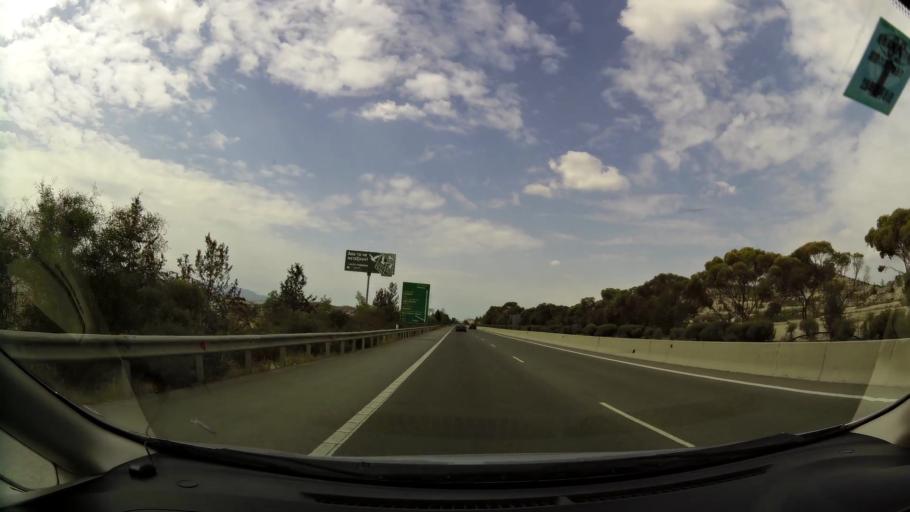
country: CY
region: Lefkosia
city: Alampra
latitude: 34.9993
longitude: 33.4107
